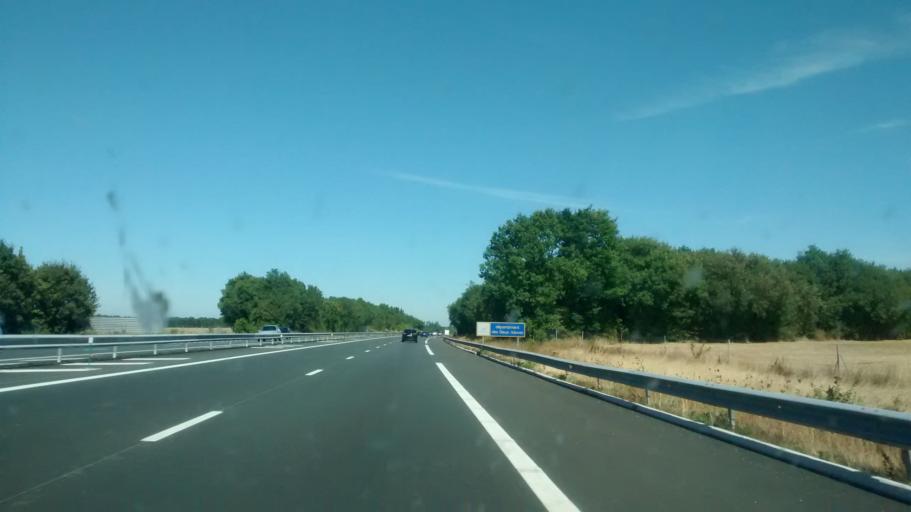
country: FR
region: Poitou-Charentes
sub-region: Departement des Deux-Sevres
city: Beauvoir-sur-Niort
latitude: 46.1352
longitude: -0.5290
